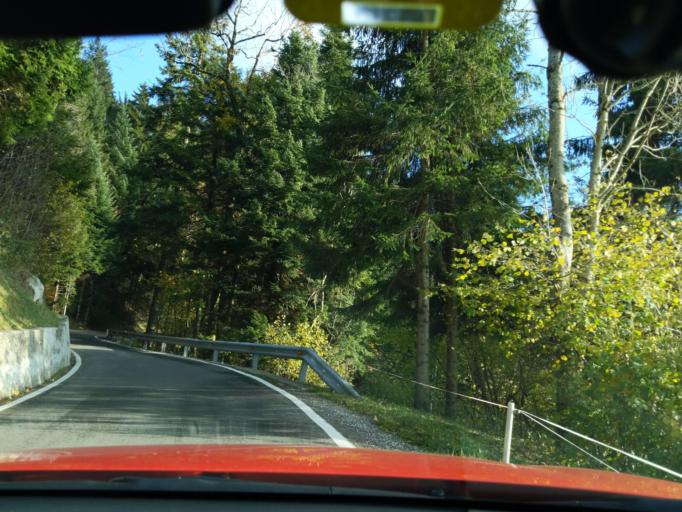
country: AT
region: Vorarlberg
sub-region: Politischer Bezirk Bregenz
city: Eichenberg
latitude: 47.5429
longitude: 9.7925
